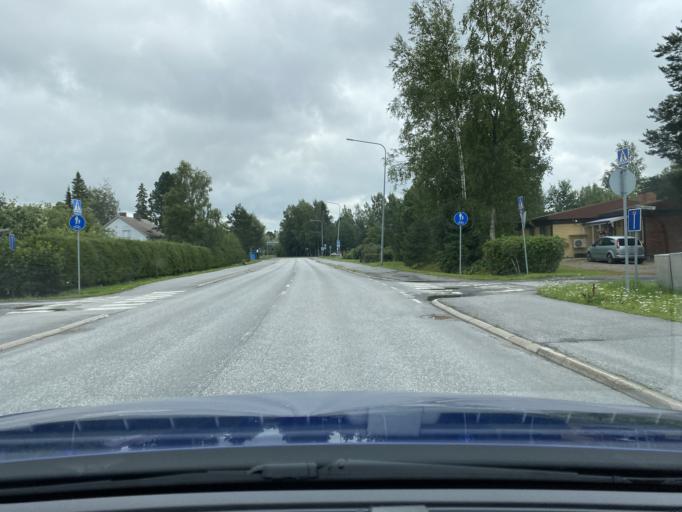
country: FI
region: Ostrobothnia
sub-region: Kyroenmaa
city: Laihia
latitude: 62.9720
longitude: 22.0232
